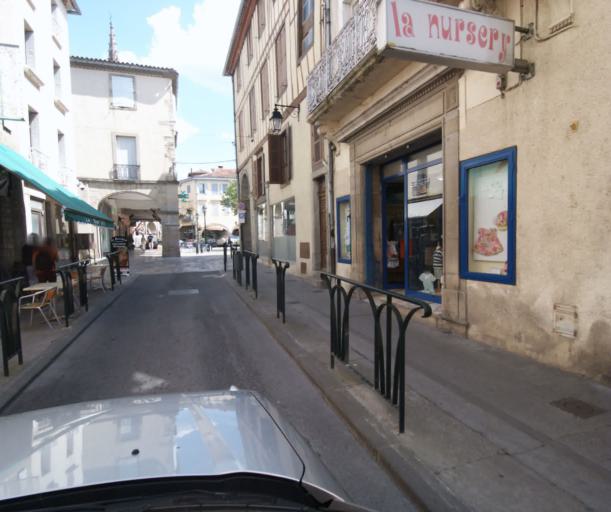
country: FR
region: Languedoc-Roussillon
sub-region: Departement de l'Aude
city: Limoux
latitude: 43.0542
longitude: 2.2174
